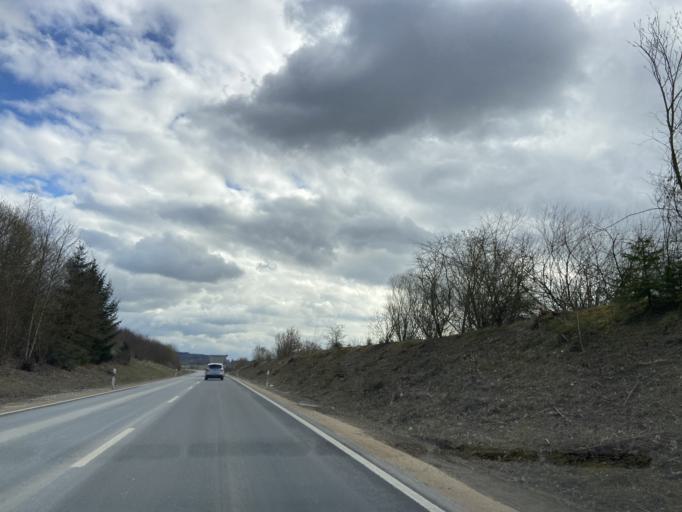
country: DE
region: Baden-Wuerttemberg
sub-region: Tuebingen Region
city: Ostrach
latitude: 47.9532
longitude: 9.3981
